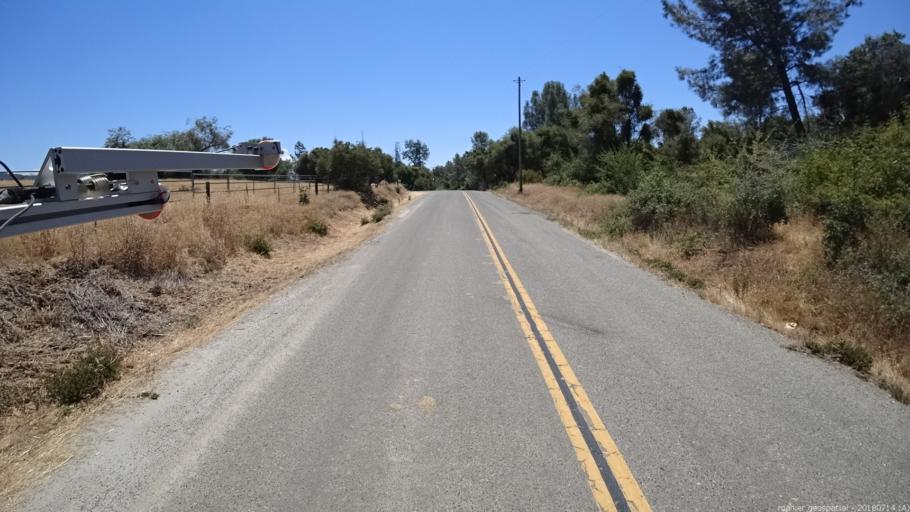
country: US
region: California
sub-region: Madera County
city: Ahwahnee
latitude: 37.3973
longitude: -119.7058
